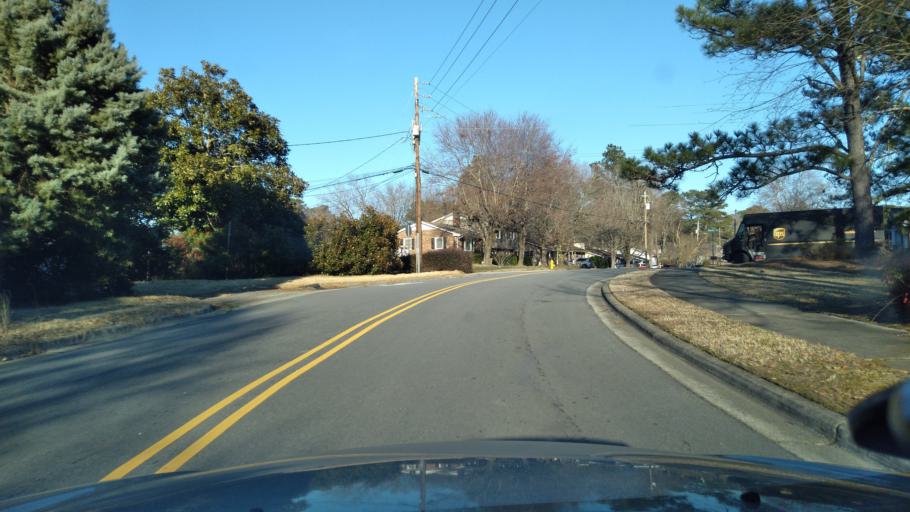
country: US
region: North Carolina
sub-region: Wake County
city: Garner
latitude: 35.6983
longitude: -78.6145
